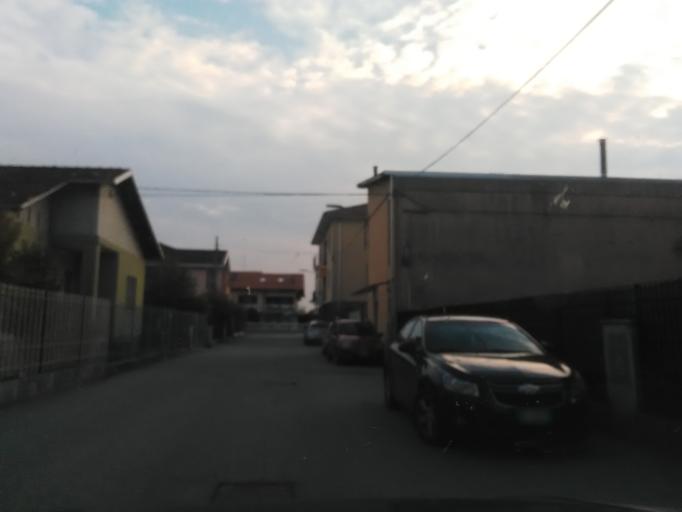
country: IT
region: Piedmont
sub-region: Provincia di Vercelli
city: Santhia
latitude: 45.3678
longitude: 8.1611
